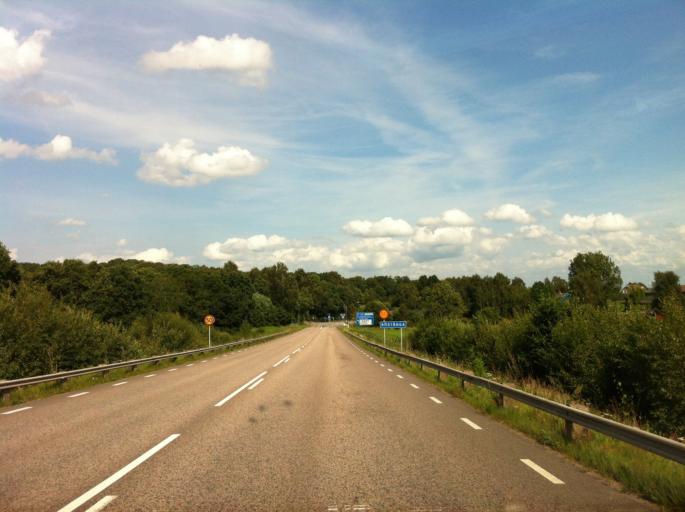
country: SE
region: Skane
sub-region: Klippans Kommun
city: Ljungbyhed
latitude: 55.9751
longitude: 13.2654
